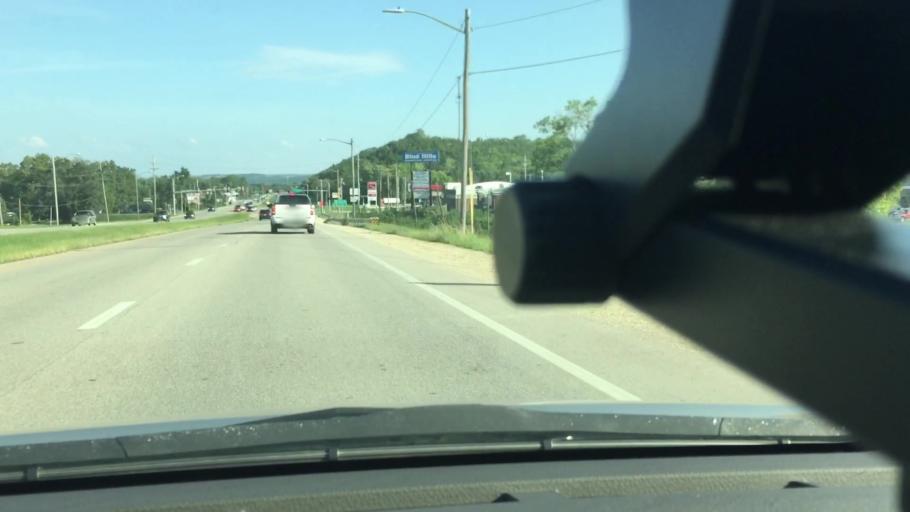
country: US
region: Kansas
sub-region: Riley County
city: Manhattan
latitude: 39.2101
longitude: -96.5735
